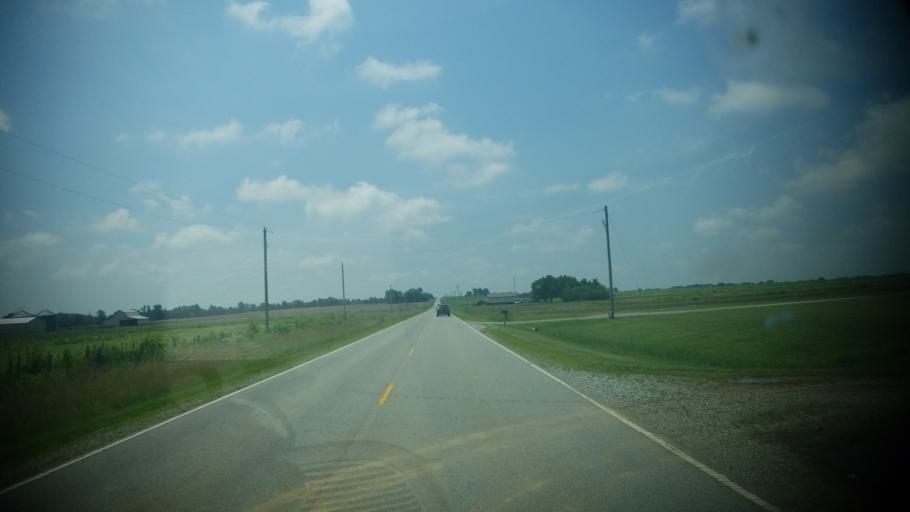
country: US
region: Illinois
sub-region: Wayne County
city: Fairfield
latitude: 38.4482
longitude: -88.3492
